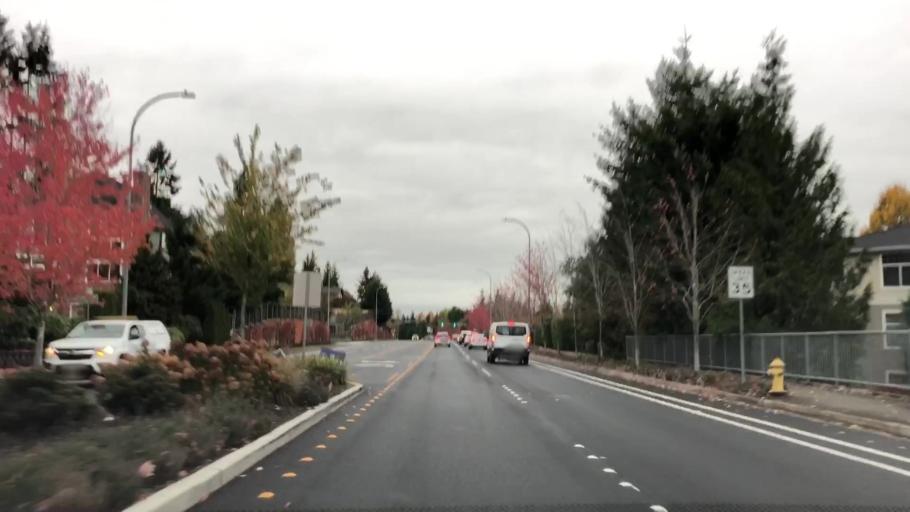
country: US
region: Washington
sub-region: King County
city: Newport
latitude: 47.5892
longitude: -122.1643
